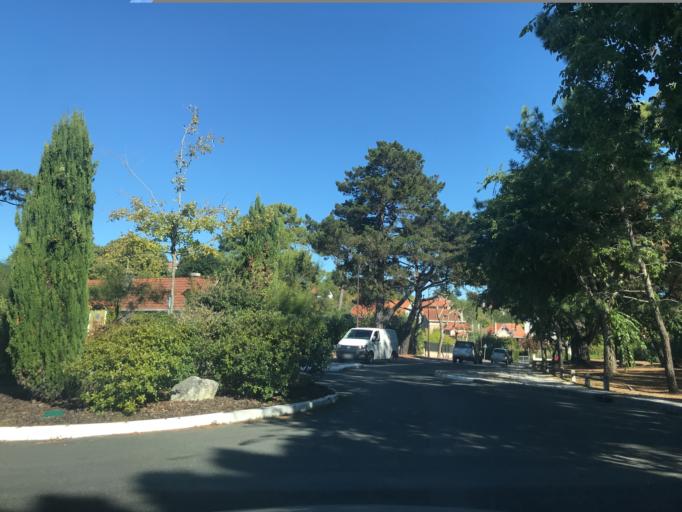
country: FR
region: Aquitaine
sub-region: Departement de la Gironde
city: Arcachon
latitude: 44.6549
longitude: -1.1793
